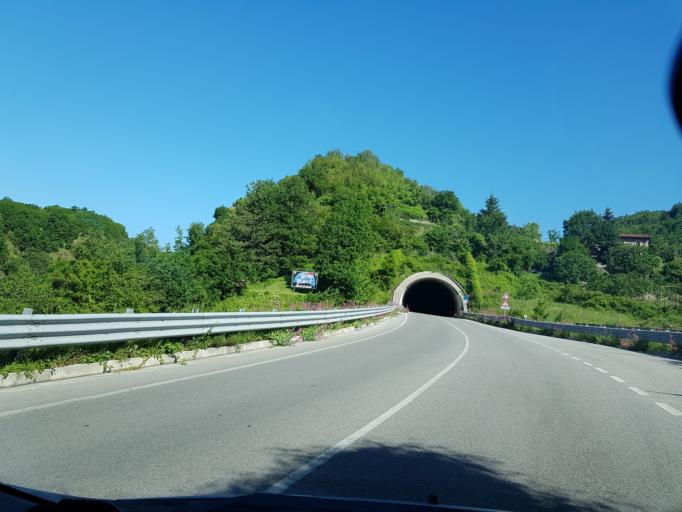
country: IT
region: Tuscany
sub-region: Provincia di Lucca
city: Piazza al Serchio-San Michele
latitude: 44.1801
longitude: 10.3099
